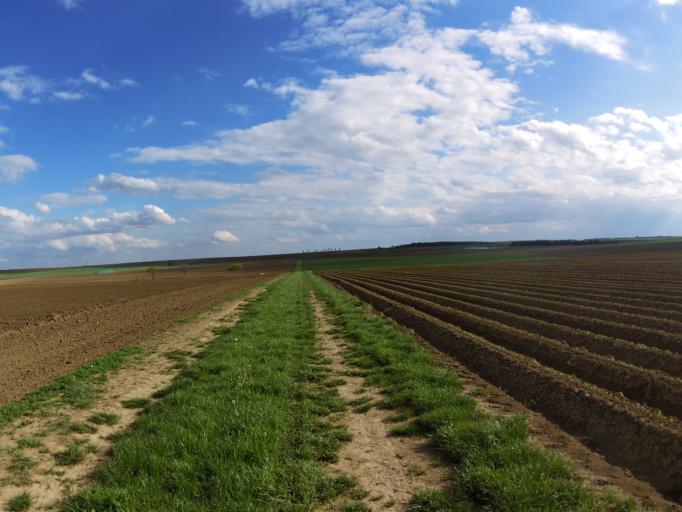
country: DE
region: Bavaria
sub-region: Regierungsbezirk Unterfranken
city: Oberpleichfeld
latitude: 49.8664
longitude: 10.0740
